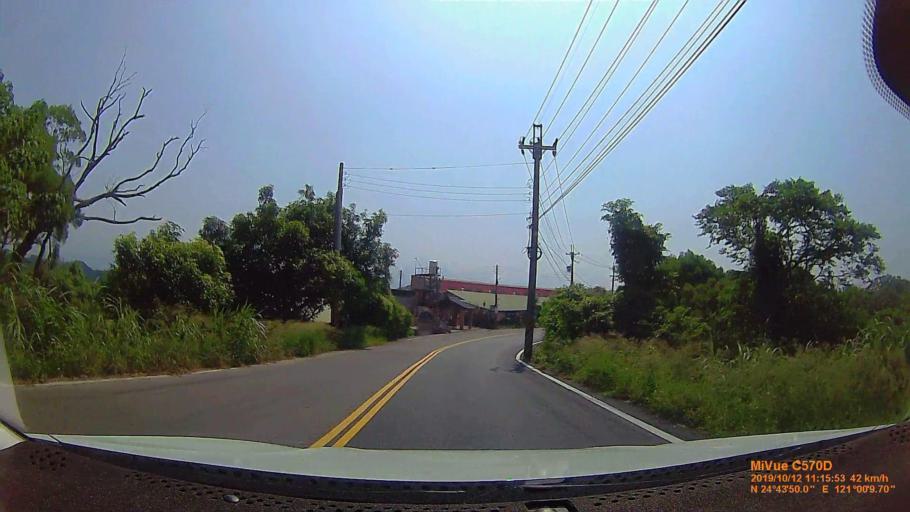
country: TW
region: Taiwan
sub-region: Hsinchu
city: Hsinchu
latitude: 24.7305
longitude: 121.0028
